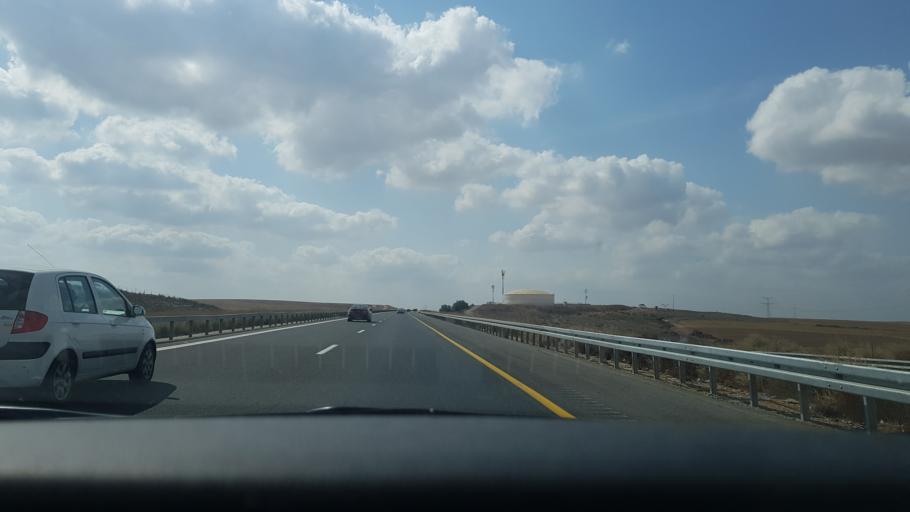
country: IL
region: Southern District
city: Qiryat Gat
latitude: 31.5464
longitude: 34.7987
